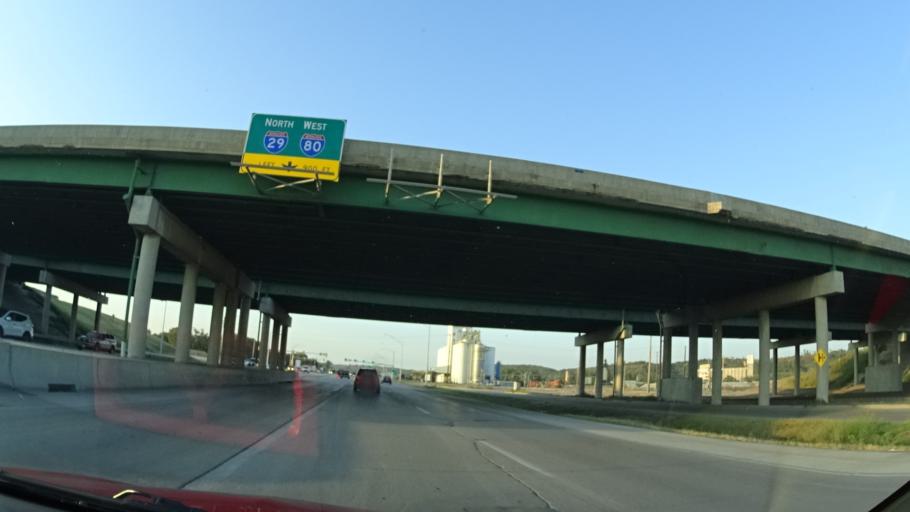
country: US
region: Iowa
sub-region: Pottawattamie County
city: Council Bluffs
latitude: 41.2316
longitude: -95.8513
